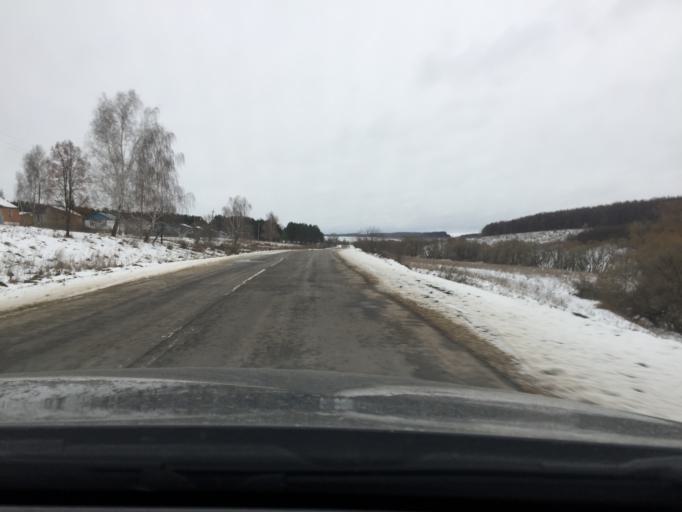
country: RU
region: Tula
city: Shchekino
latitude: 53.8255
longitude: 37.5586
